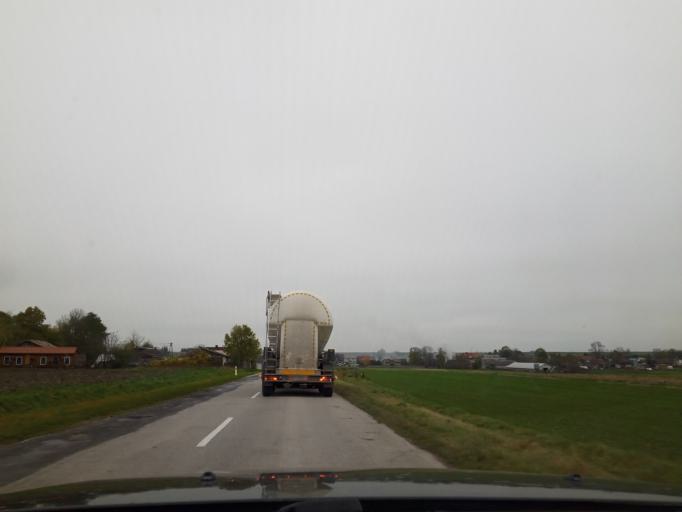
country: PL
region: Swietokrzyskie
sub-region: Powiat jedrzejowski
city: Jedrzejow
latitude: 50.5864
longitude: 20.3186
